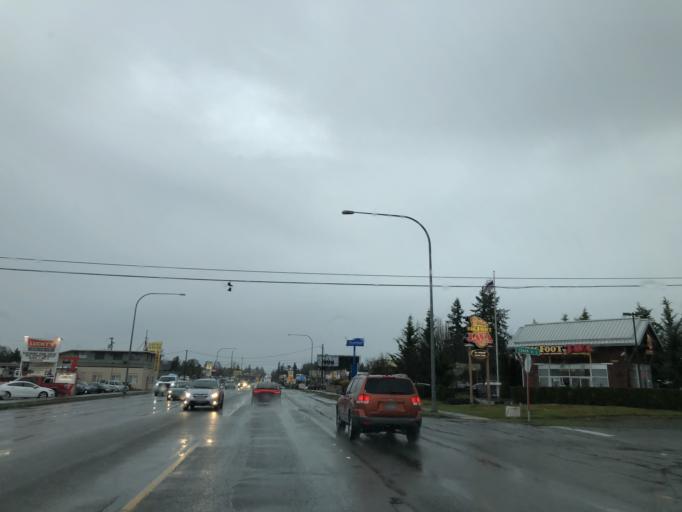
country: US
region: Washington
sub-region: Pierce County
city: Parkland
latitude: 47.1330
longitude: -122.4346
